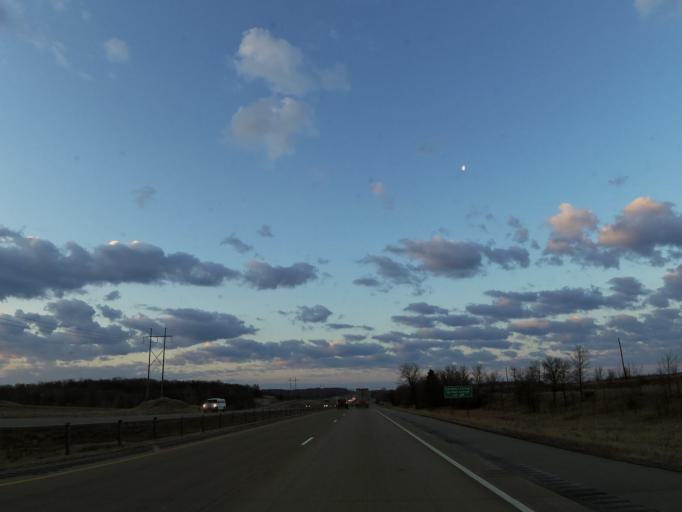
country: US
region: Minnesota
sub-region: Scott County
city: Elko New Market
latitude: 44.4886
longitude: -93.2920
